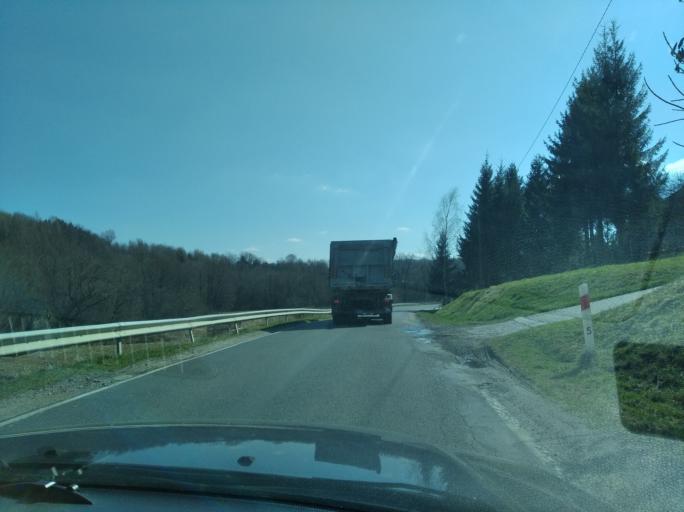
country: PL
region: Subcarpathian Voivodeship
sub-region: Powiat przeworski
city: Jawornik Polski
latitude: 49.9066
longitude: 22.3071
